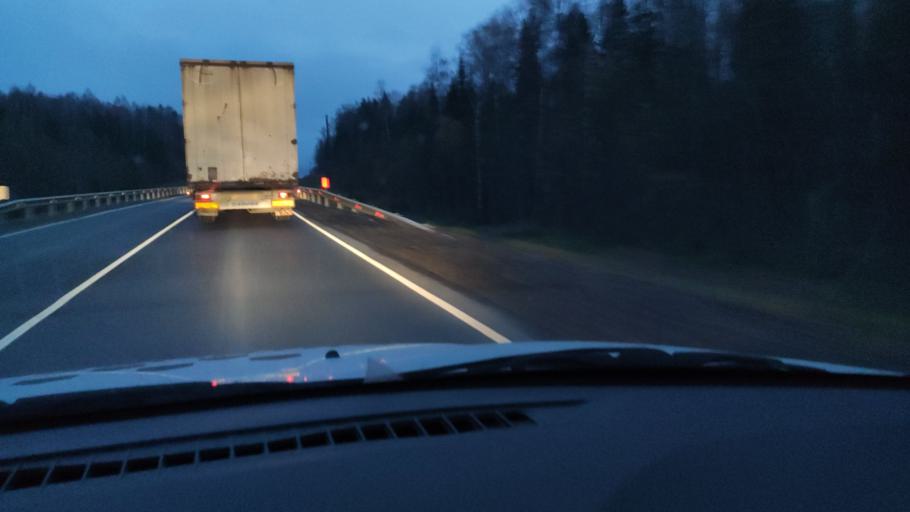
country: RU
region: Kirov
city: Kostino
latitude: 58.8338
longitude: 53.4997
